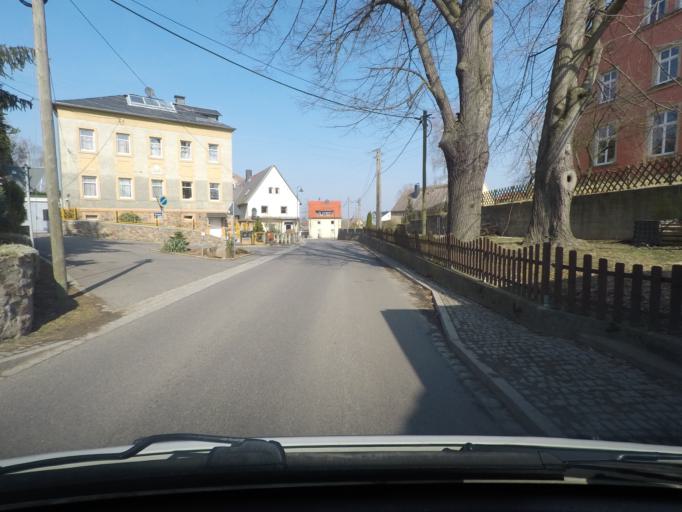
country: DE
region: Saxony
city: Coswig
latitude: 51.0854
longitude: 13.5839
